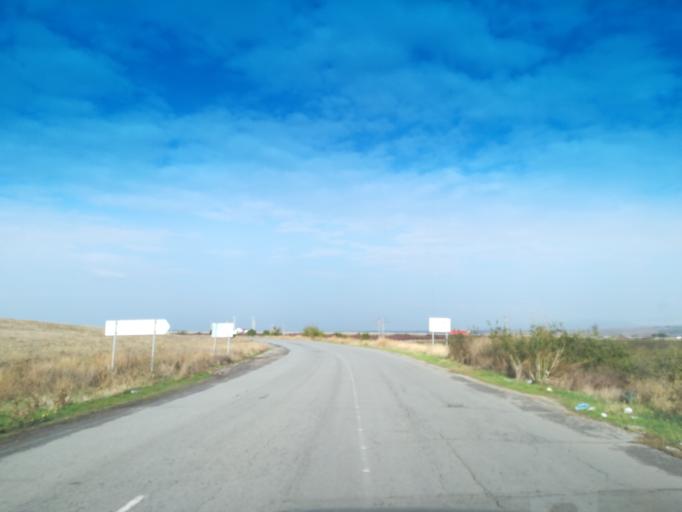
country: BG
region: Stara Zagora
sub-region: Obshtina Chirpan
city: Chirpan
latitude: 42.2054
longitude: 25.3082
